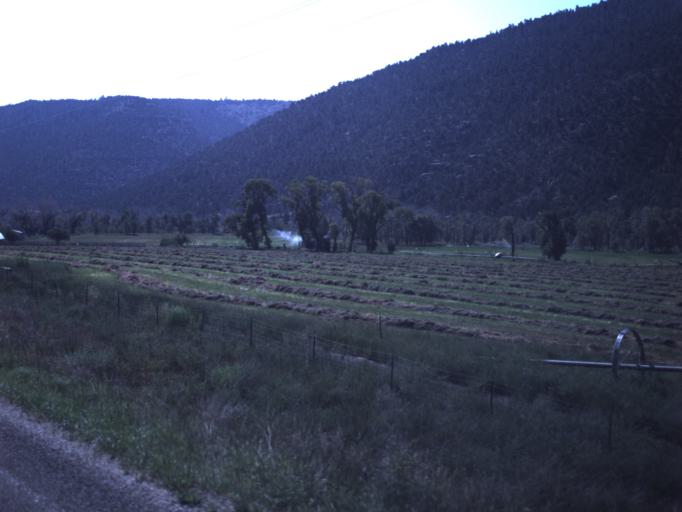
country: US
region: Utah
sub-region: Duchesne County
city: Duchesne
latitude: 40.3024
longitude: -110.6112
